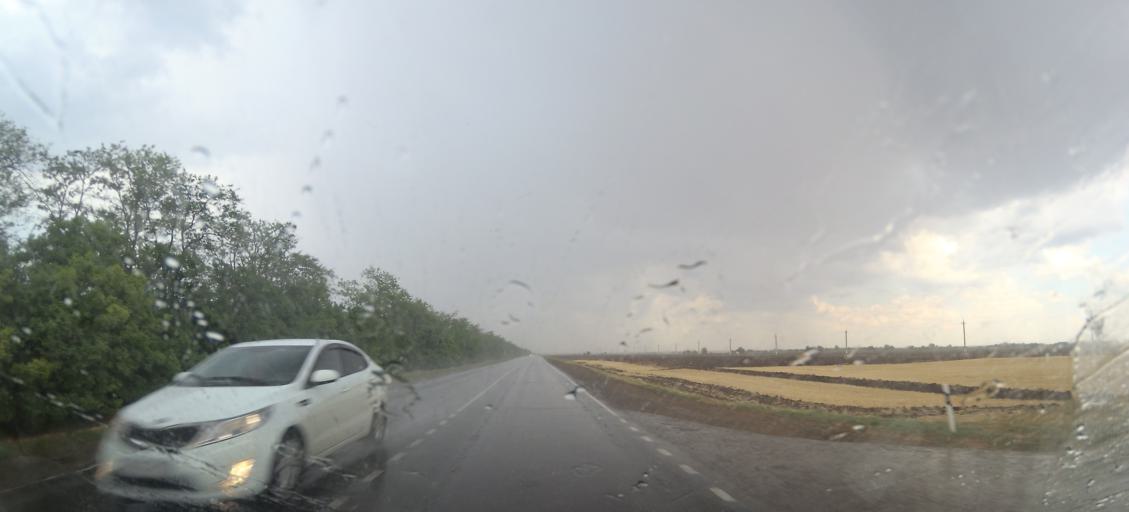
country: RU
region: Rostov
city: Proletarsk
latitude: 46.6510
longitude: 41.6778
